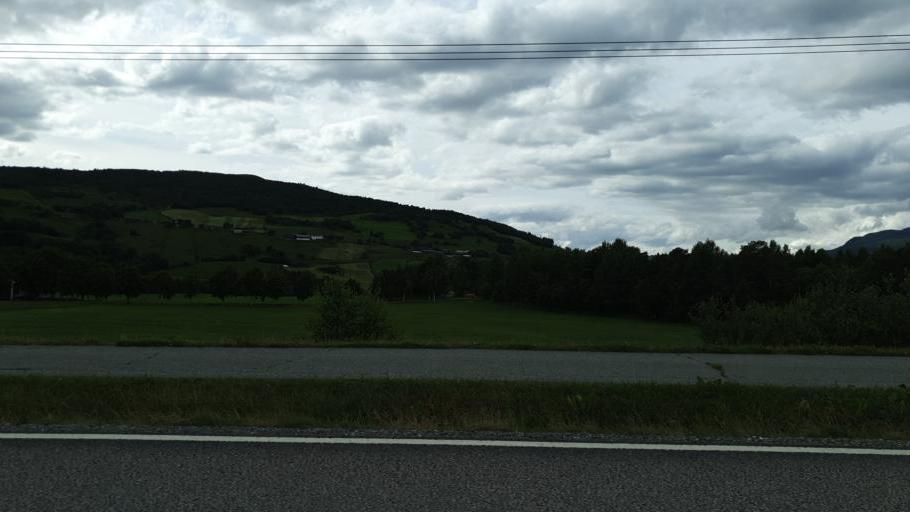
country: NO
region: Sor-Trondelag
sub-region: Oppdal
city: Oppdal
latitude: 62.5747
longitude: 9.6508
